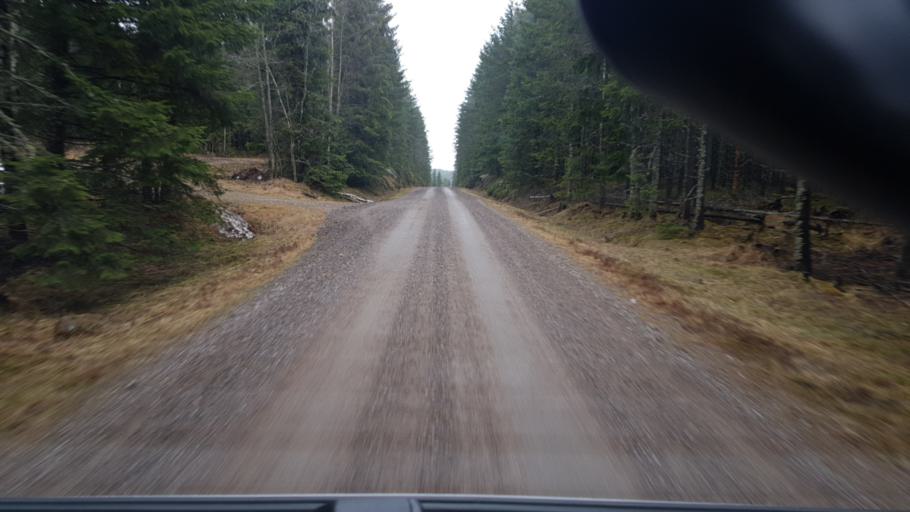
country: SE
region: Vaermland
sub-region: Eda Kommun
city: Charlottenberg
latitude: 60.0112
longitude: 12.5060
